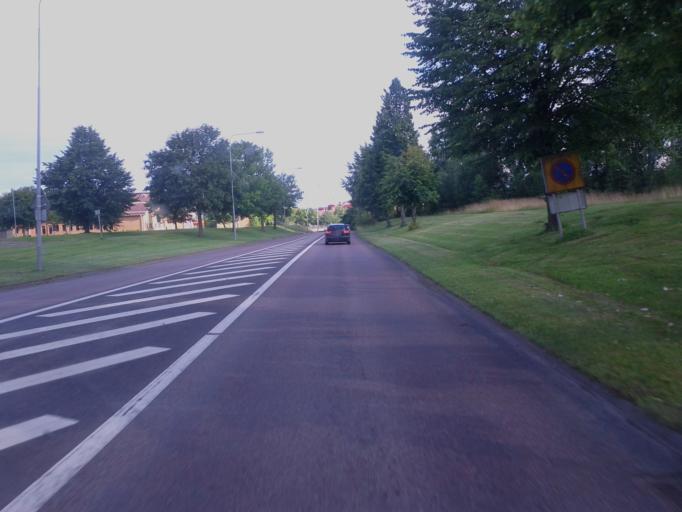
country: SE
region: Dalarna
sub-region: Borlange Kommun
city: Borlaenge
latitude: 60.4924
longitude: 15.4330
